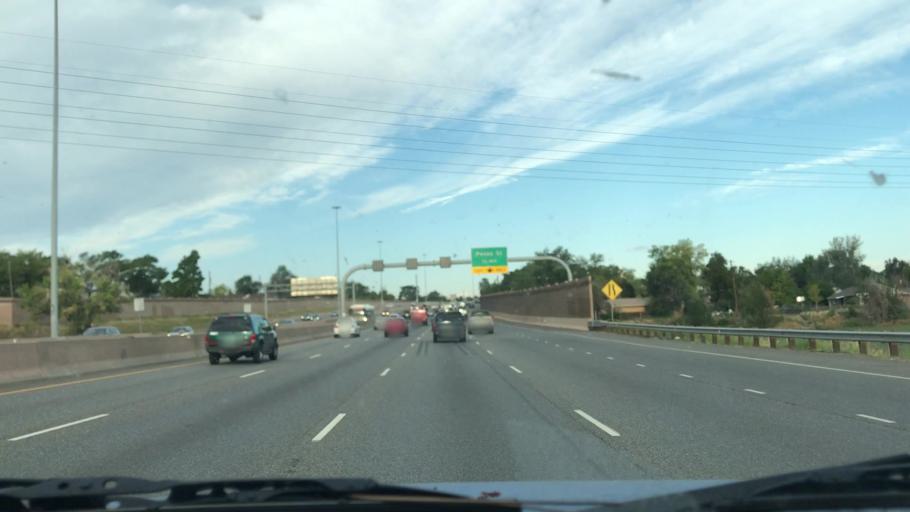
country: US
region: Colorado
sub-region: Adams County
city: Twin Lakes
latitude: 39.8277
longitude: -104.9910
